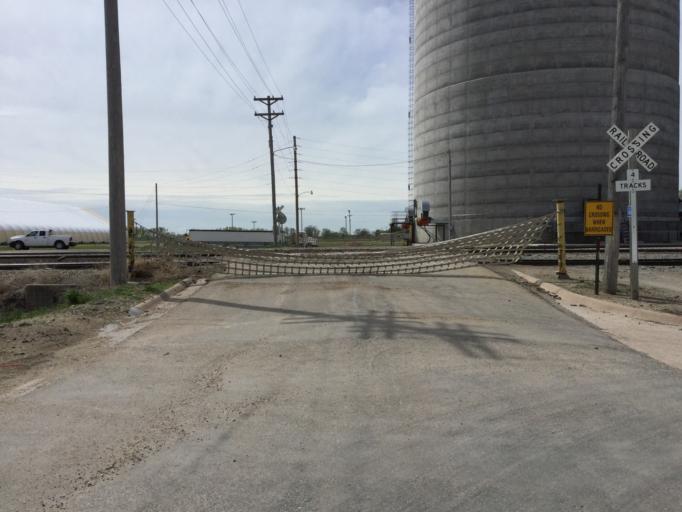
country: US
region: Kansas
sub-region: Osborne County
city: Osborne
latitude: 39.5028
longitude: -98.5393
